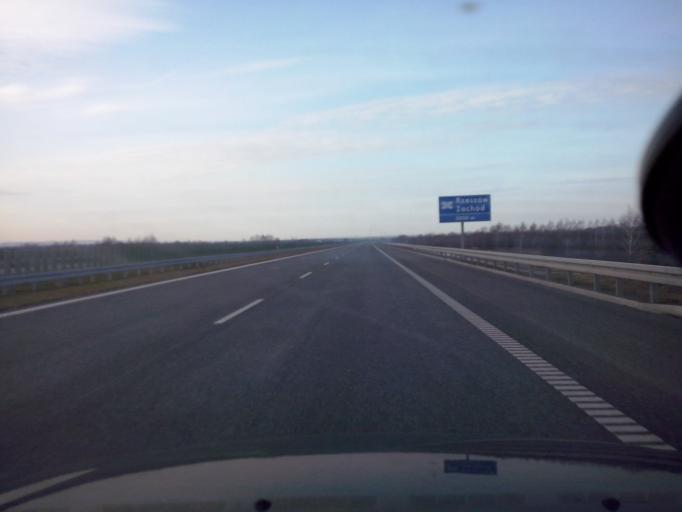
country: PL
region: Subcarpathian Voivodeship
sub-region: Powiat rzeszowski
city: Rudna Mala
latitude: 50.1072
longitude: 21.9664
